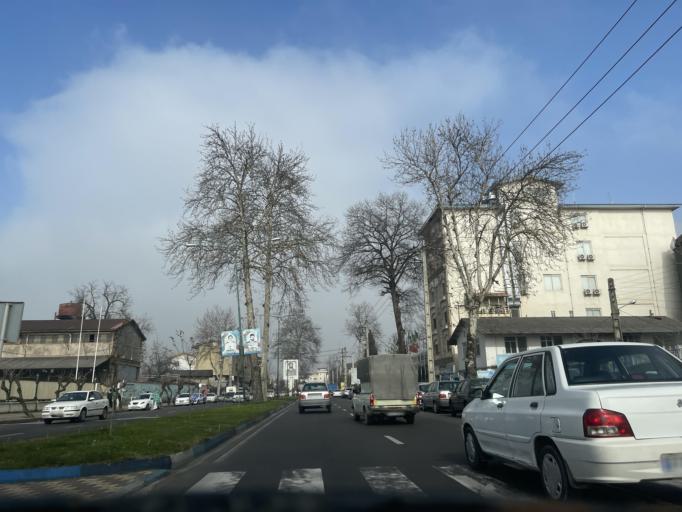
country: IR
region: Gilan
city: Rasht
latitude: 37.2723
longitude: 49.6085
